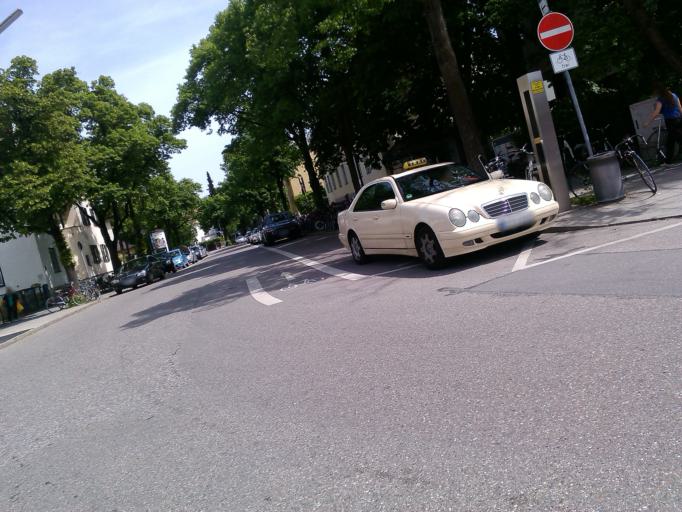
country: DE
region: Bavaria
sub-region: Upper Bavaria
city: Pasing
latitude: 48.1506
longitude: 11.4621
